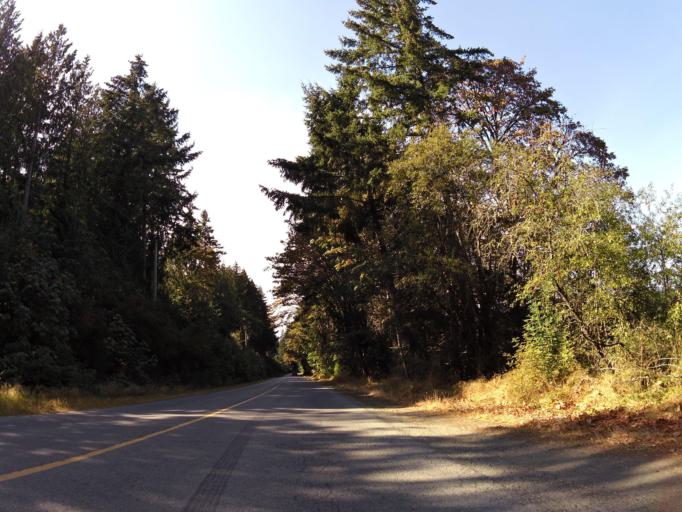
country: CA
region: British Columbia
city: North Saanich
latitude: 48.6909
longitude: -123.5585
